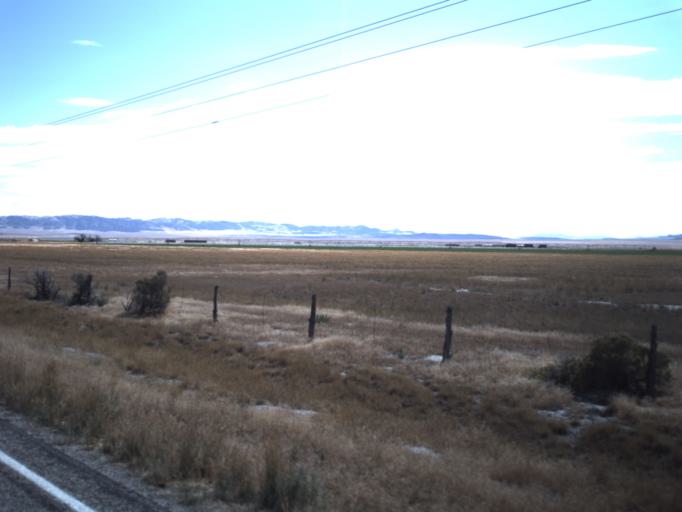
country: US
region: Idaho
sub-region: Oneida County
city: Malad City
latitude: 41.9664
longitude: -112.9309
